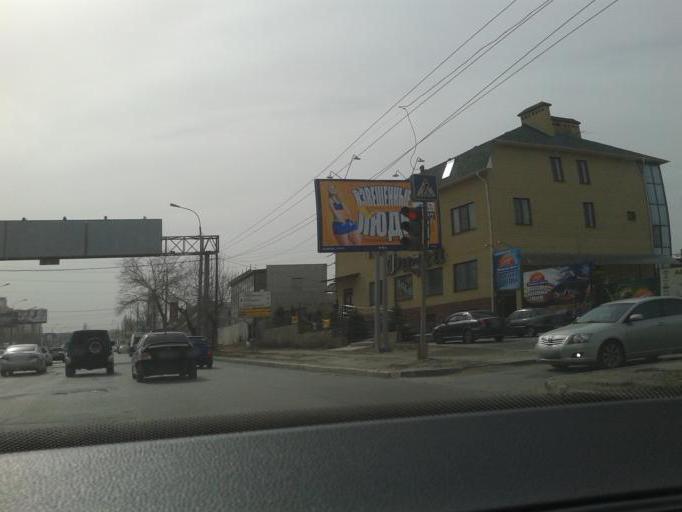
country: RU
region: Volgograd
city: Volgograd
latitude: 48.7060
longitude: 44.4849
